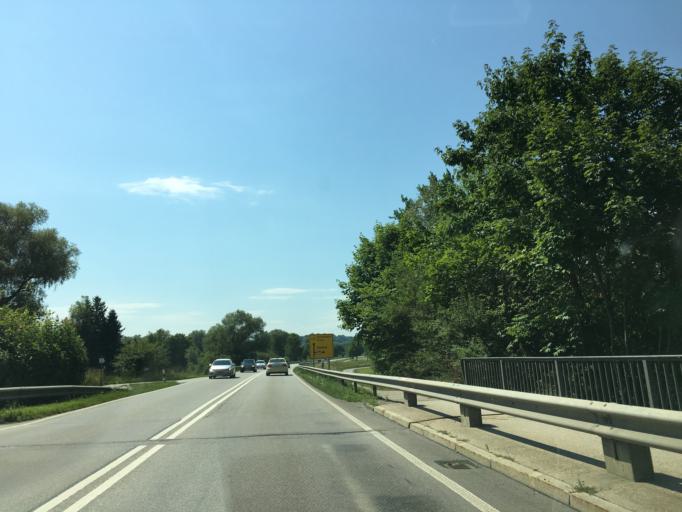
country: DE
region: Bavaria
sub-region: Upper Bavaria
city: Ramerberg
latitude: 48.0219
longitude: 12.1730
